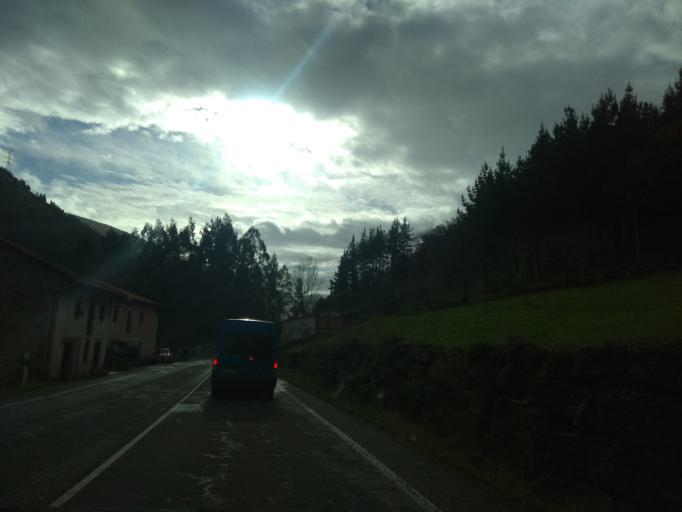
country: ES
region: Cantabria
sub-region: Provincia de Cantabria
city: San Pedro del Romeral
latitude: 43.1522
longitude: -3.8976
